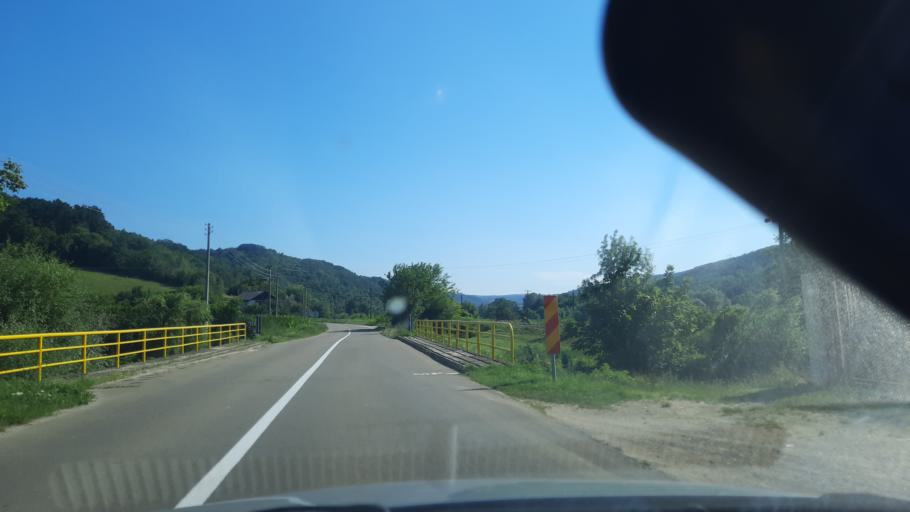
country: RS
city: Turija
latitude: 44.5203
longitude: 21.6399
